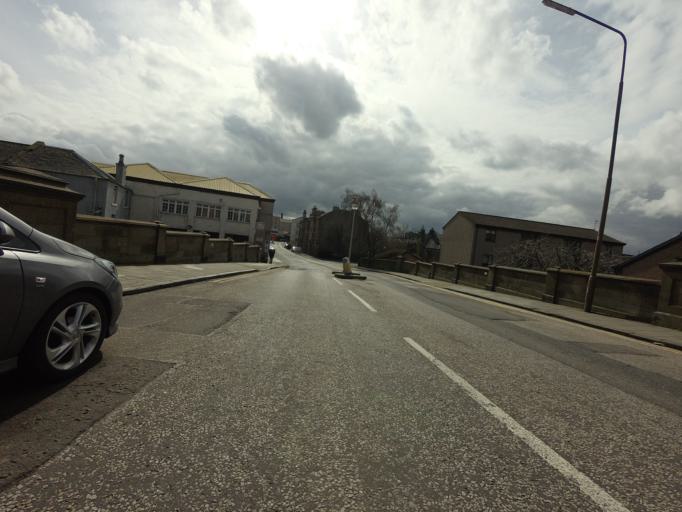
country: GB
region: Scotland
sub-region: Edinburgh
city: Edinburgh
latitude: 55.9717
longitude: -3.1875
